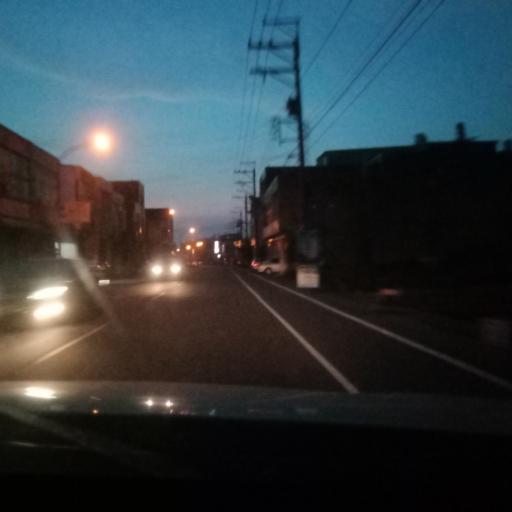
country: TW
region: Taiwan
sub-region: Hsinchu
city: Zhubei
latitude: 24.9005
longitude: 121.0546
